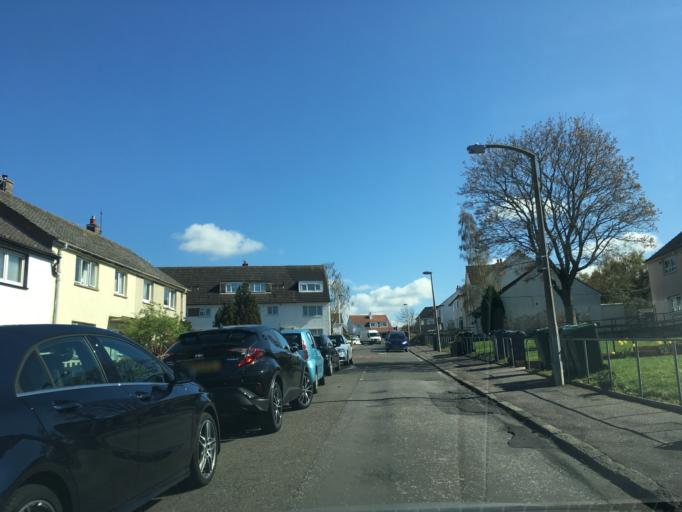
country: GB
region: Scotland
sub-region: Edinburgh
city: Colinton
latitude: 55.9040
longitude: -3.2209
